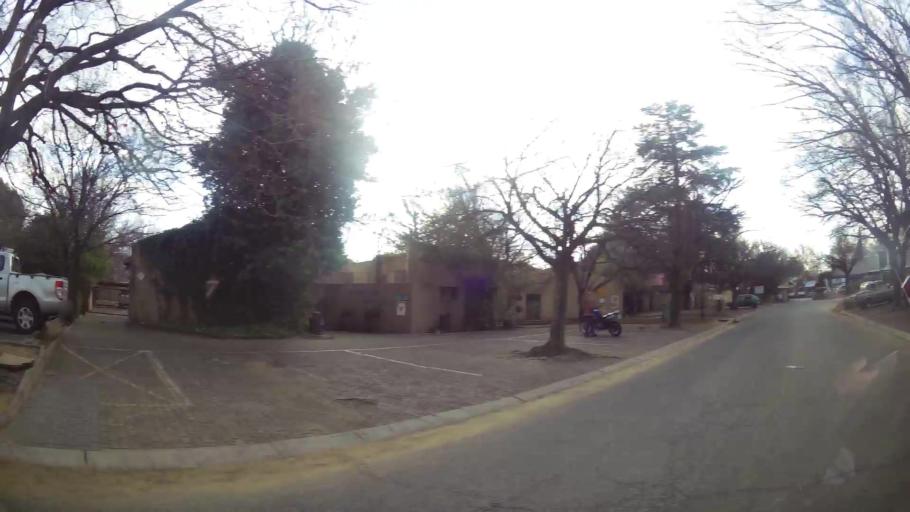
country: ZA
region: Orange Free State
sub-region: Fezile Dabi District Municipality
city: Sasolburg
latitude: -26.8113
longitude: 27.8257
